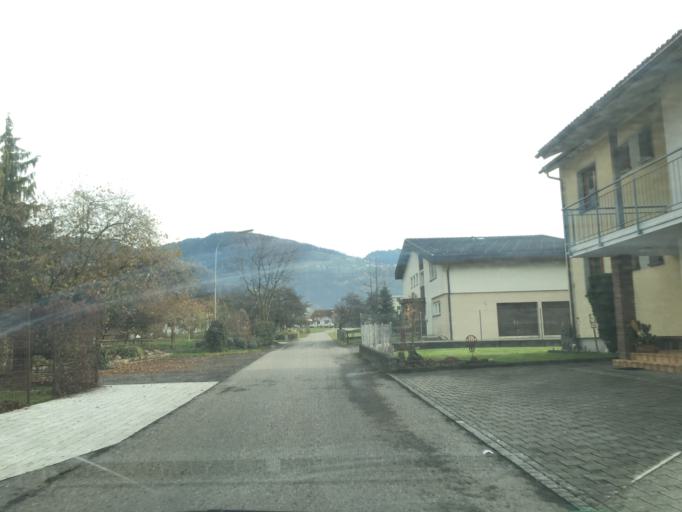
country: AT
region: Vorarlberg
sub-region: Politischer Bezirk Feldkirch
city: Klaus
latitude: 47.3086
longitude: 9.6390
